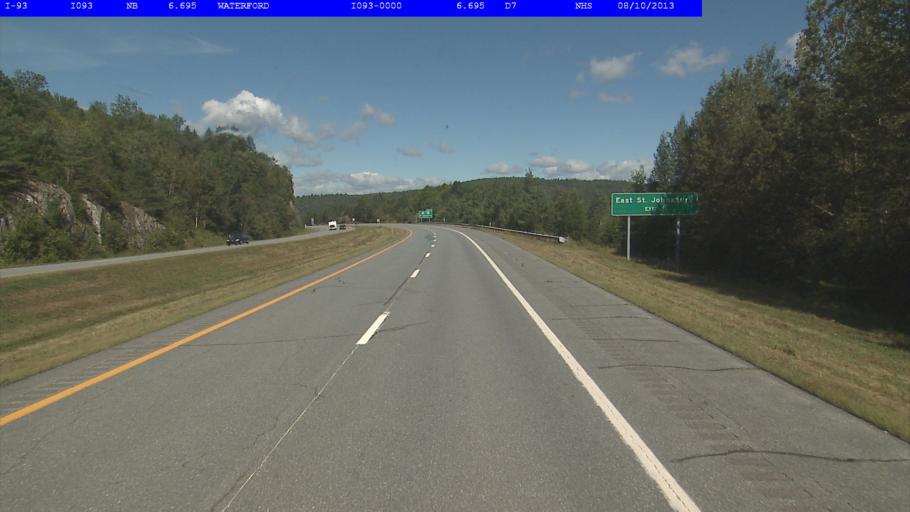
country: US
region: Vermont
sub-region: Caledonia County
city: St Johnsbury
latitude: 44.4259
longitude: -71.9404
